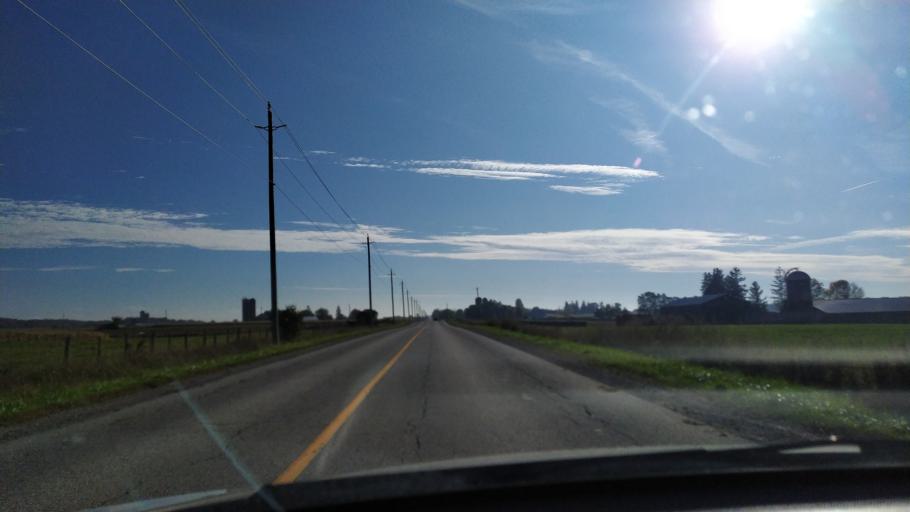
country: CA
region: Ontario
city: Waterloo
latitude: 43.4924
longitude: -80.7232
